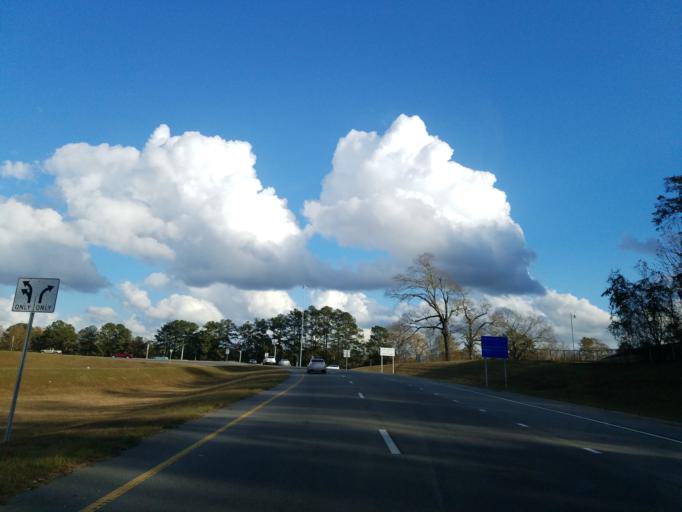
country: US
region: Mississippi
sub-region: Jones County
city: Laurel
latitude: 31.6832
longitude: -89.1486
